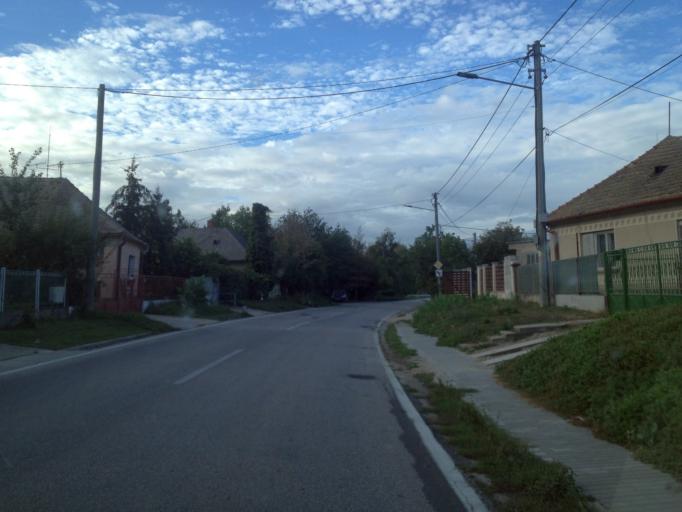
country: HU
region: Komarom-Esztergom
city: Almasfuzito
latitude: 47.7504
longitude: 18.2212
